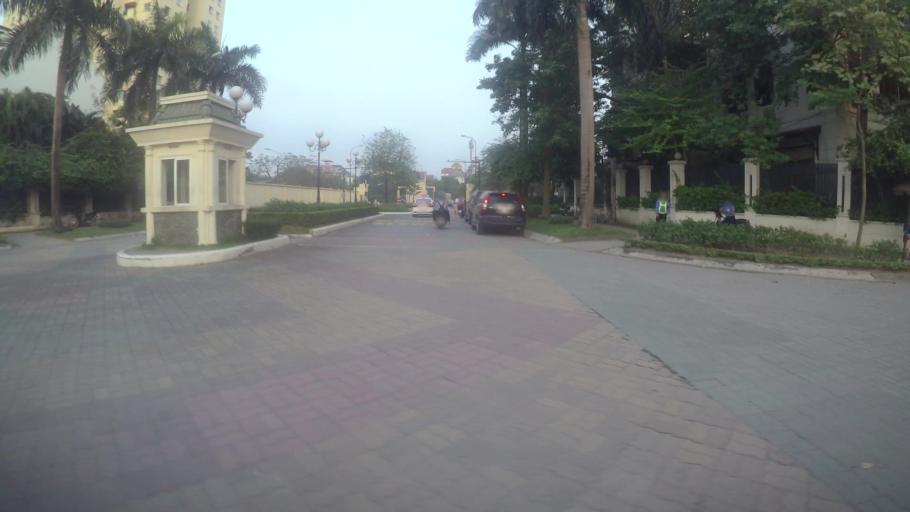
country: VN
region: Ha Noi
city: Tay Ho
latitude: 21.0735
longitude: 105.8087
